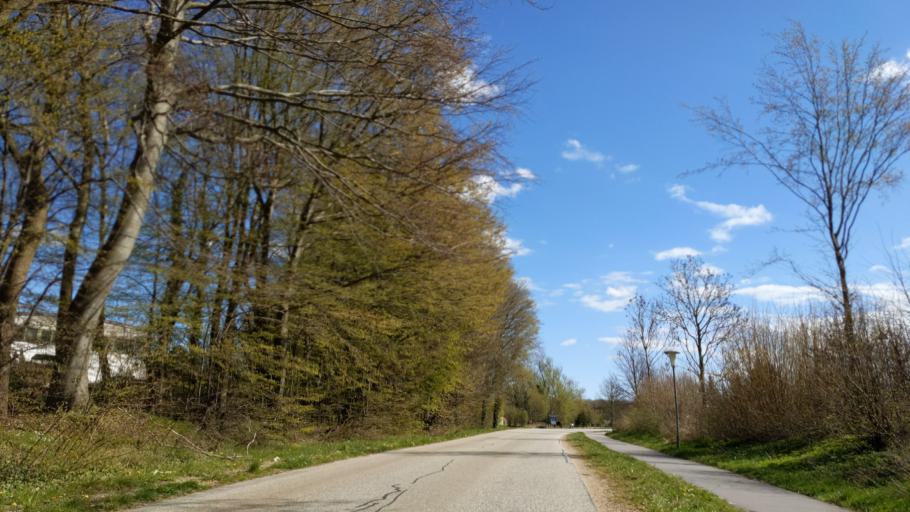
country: DE
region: Mecklenburg-Vorpommern
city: Selmsdorf
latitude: 53.8874
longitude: 10.8883
